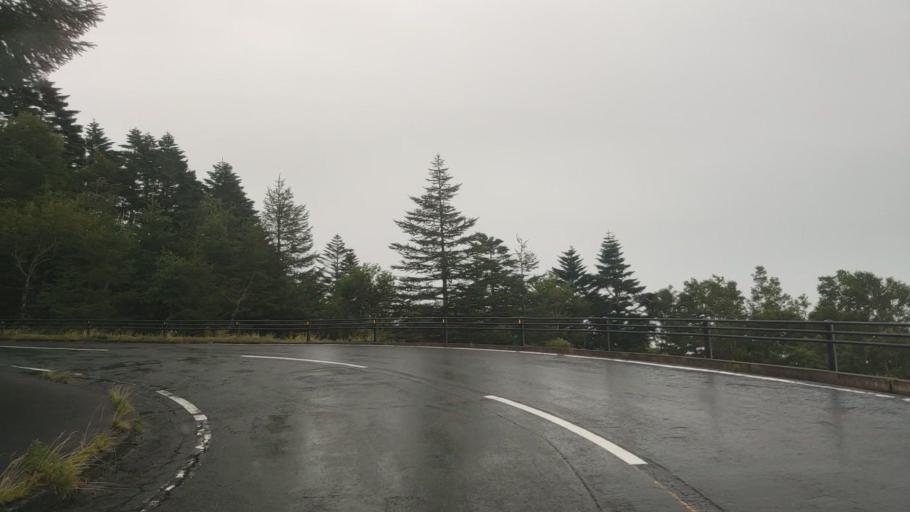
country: JP
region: Shizuoka
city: Fujinomiya
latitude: 35.3257
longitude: 138.7332
